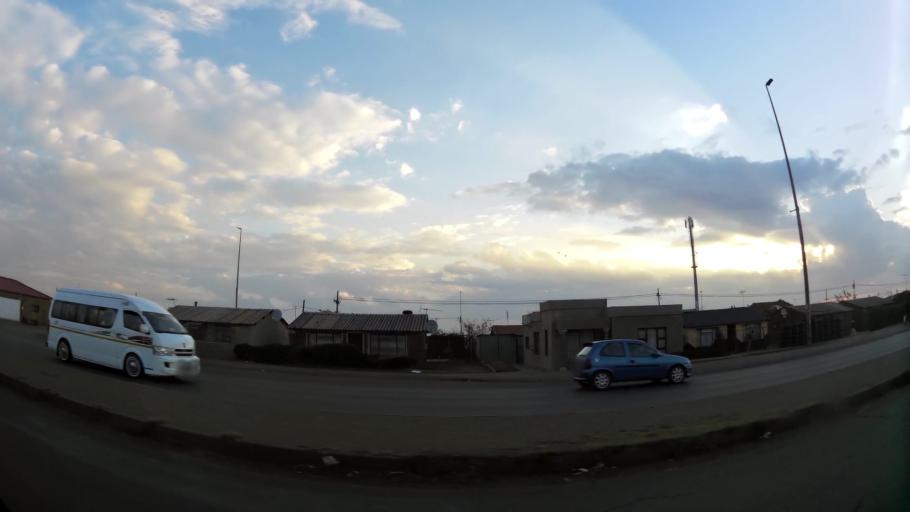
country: ZA
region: Gauteng
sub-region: City of Johannesburg Metropolitan Municipality
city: Orange Farm
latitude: -26.5664
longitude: 27.8353
